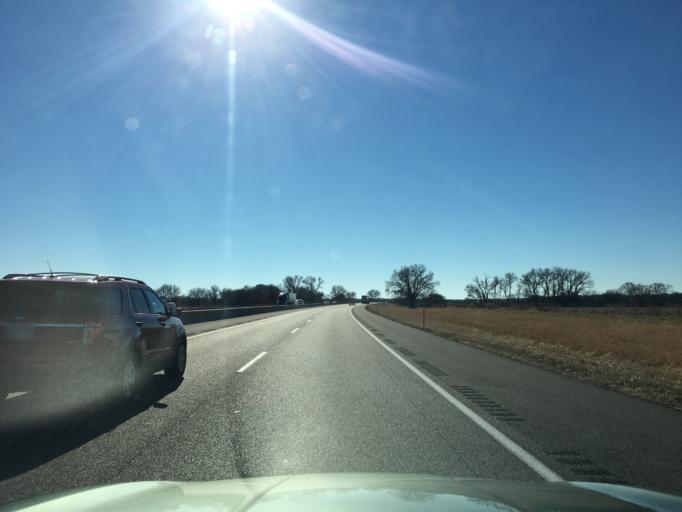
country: US
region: Kansas
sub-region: Sumner County
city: Belle Plaine
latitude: 37.4182
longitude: -97.3212
